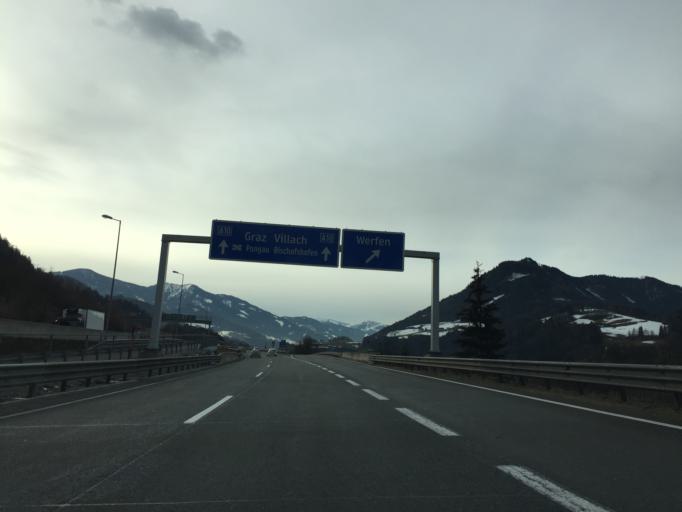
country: AT
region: Salzburg
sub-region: Politischer Bezirk Sankt Johann im Pongau
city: Werfen
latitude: 47.4717
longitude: 13.1983
